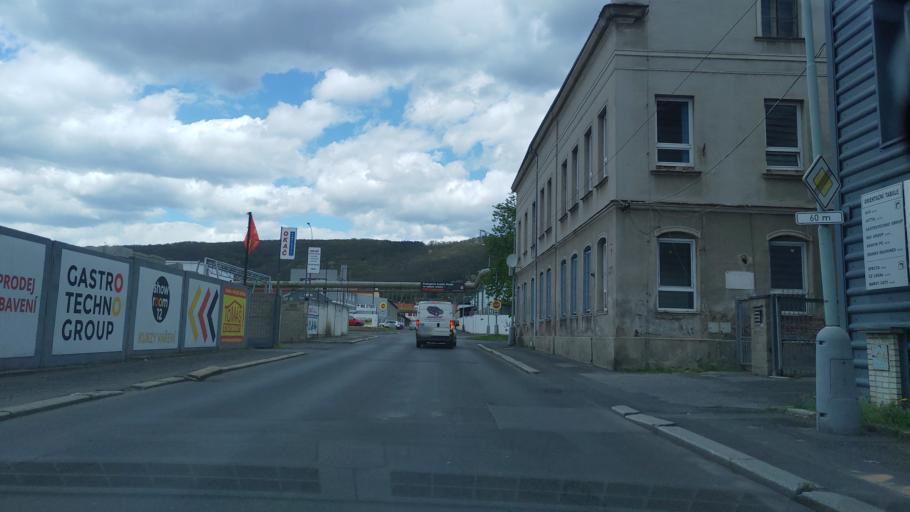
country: CZ
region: Ustecky
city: Trmice
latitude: 50.6586
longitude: 14.0062
